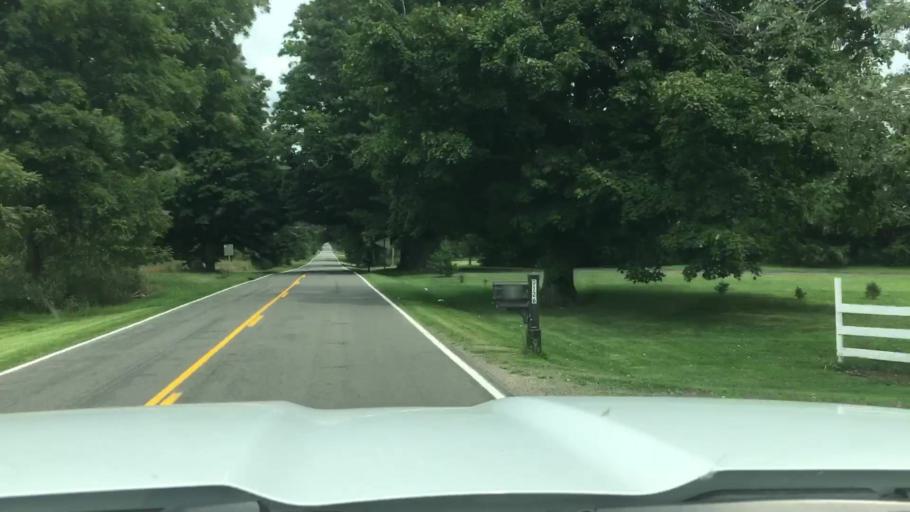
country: US
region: Michigan
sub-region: Ingham County
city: Webberville
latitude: 42.6764
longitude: -84.1892
